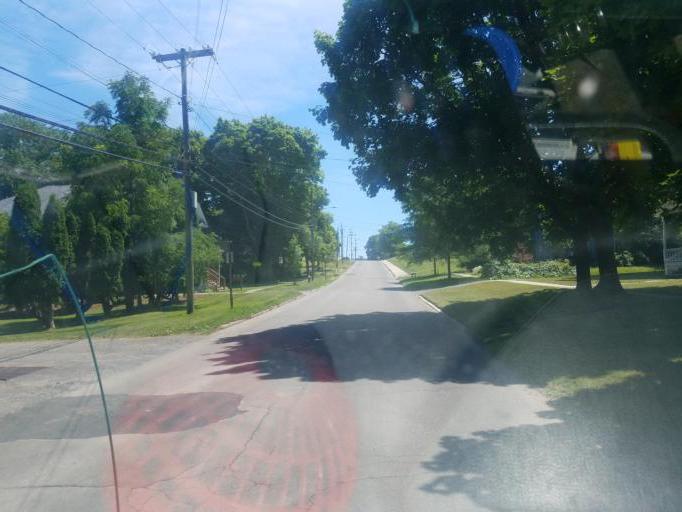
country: US
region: New York
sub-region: Yates County
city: Penn Yan
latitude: 42.6542
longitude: -77.0433
